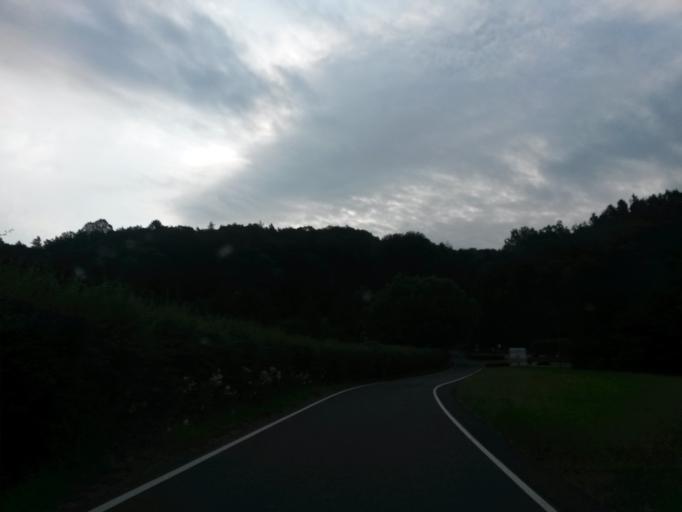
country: DE
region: North Rhine-Westphalia
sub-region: Regierungsbezirk Koln
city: Overath
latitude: 50.9629
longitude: 7.2565
